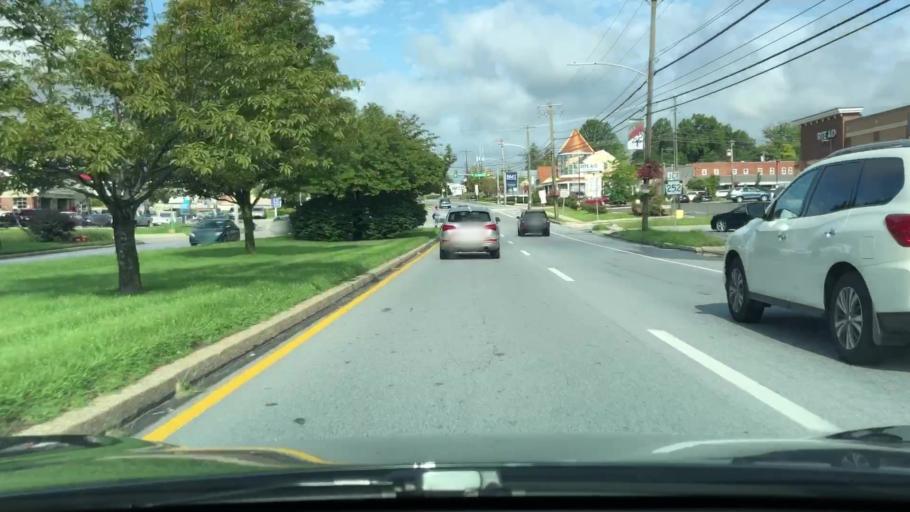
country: US
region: Pennsylvania
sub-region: Delaware County
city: Broomall
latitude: 39.9864
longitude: -75.3976
